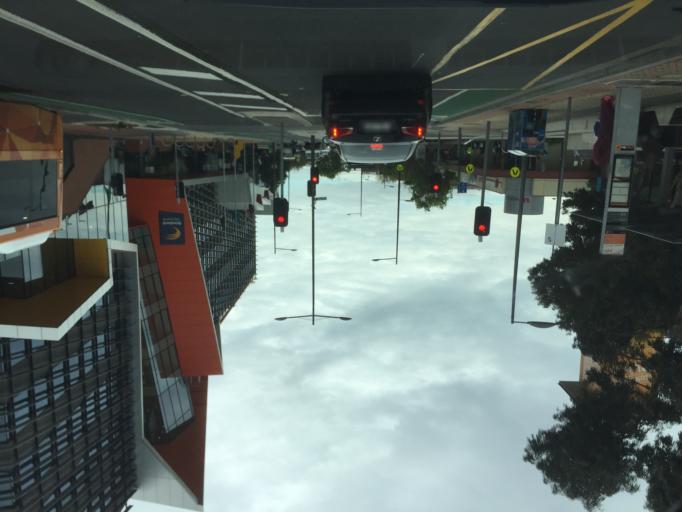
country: AU
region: Victoria
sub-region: Brimbank
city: Sunshine North
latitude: -37.7826
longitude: 144.8325
